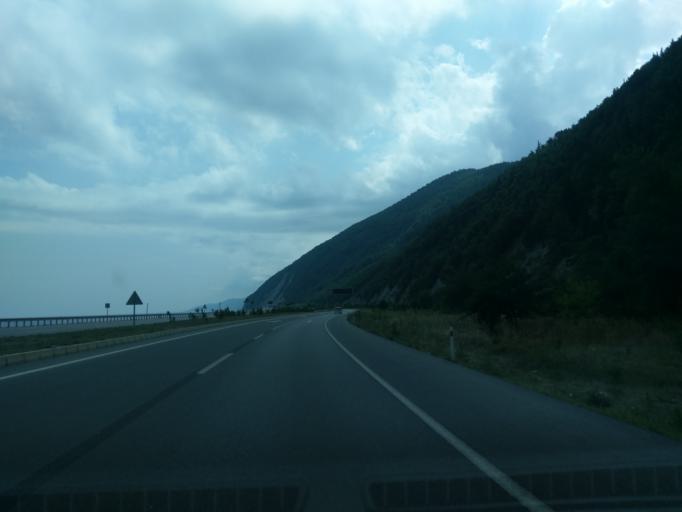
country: TR
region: Sinop
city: Gerze
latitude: 41.7503
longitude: 35.2392
